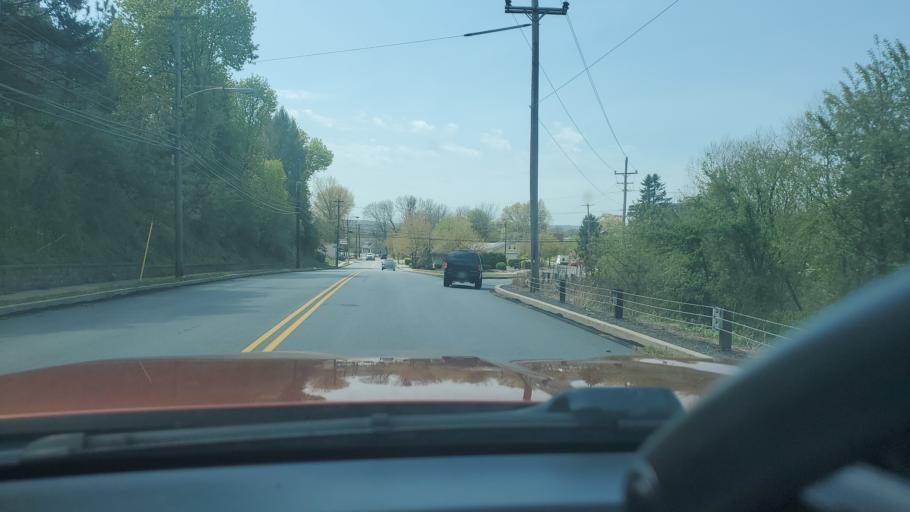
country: US
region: Pennsylvania
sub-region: Montgomery County
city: Pottstown
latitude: 40.2586
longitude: -75.6452
